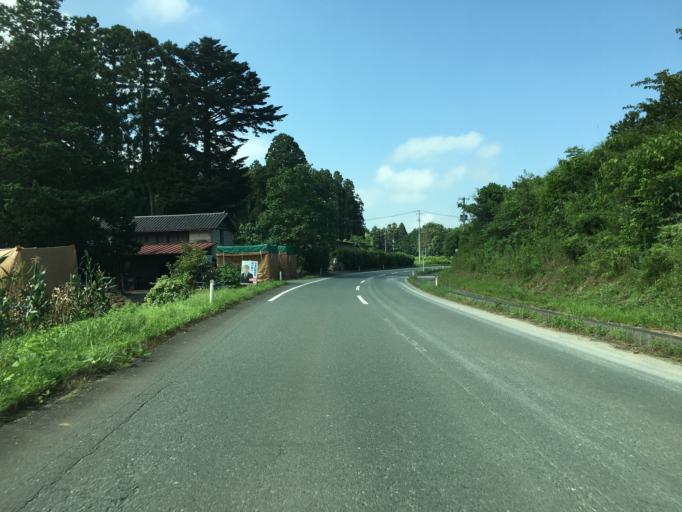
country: JP
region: Miyagi
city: Marumori
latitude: 37.8765
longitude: 140.8873
